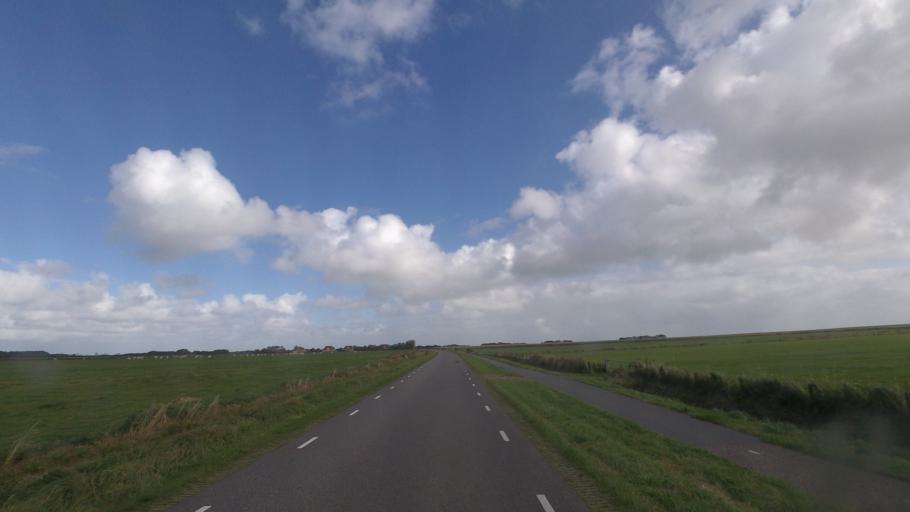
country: NL
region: Friesland
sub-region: Gemeente Ameland
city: Hollum
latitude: 53.4379
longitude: 5.6456
